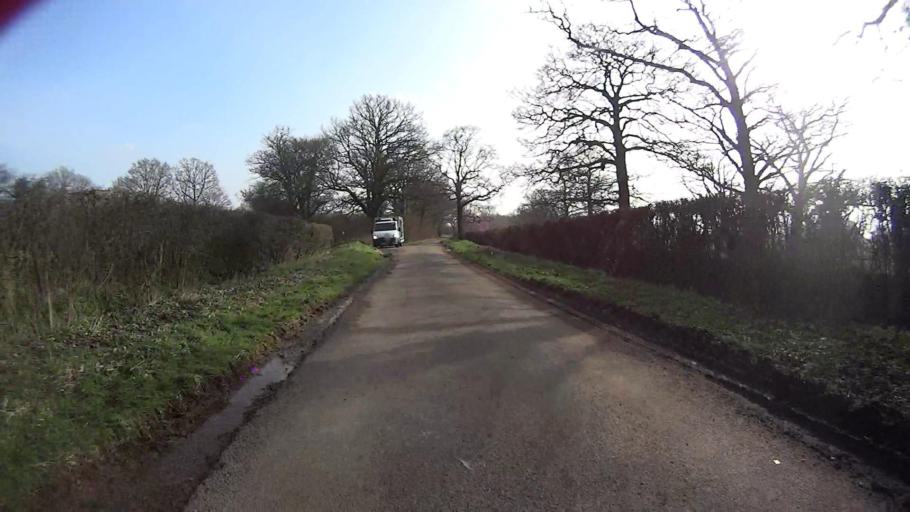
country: GB
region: England
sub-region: West Sussex
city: Copthorne
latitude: 51.1812
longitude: -0.1024
